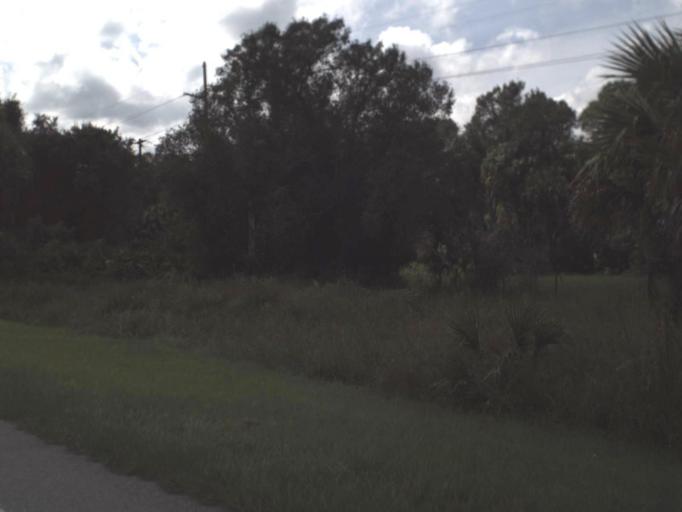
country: US
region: Florida
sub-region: Collier County
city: Immokalee
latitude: 26.3078
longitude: -81.3428
